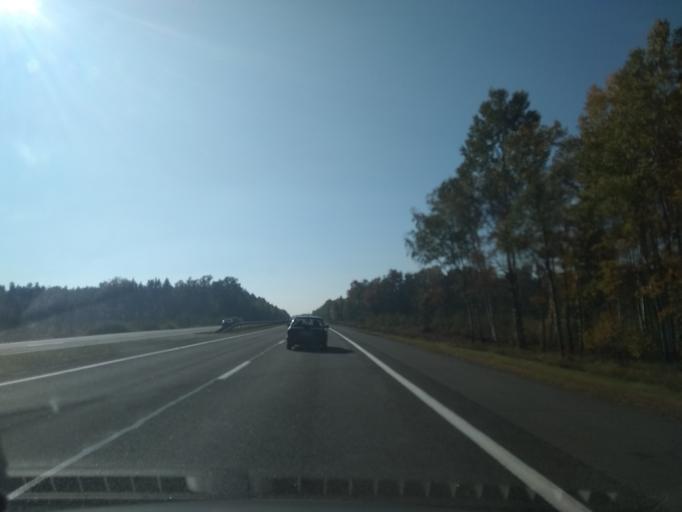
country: BY
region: Brest
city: Ivatsevichy
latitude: 52.8228
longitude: 25.5893
